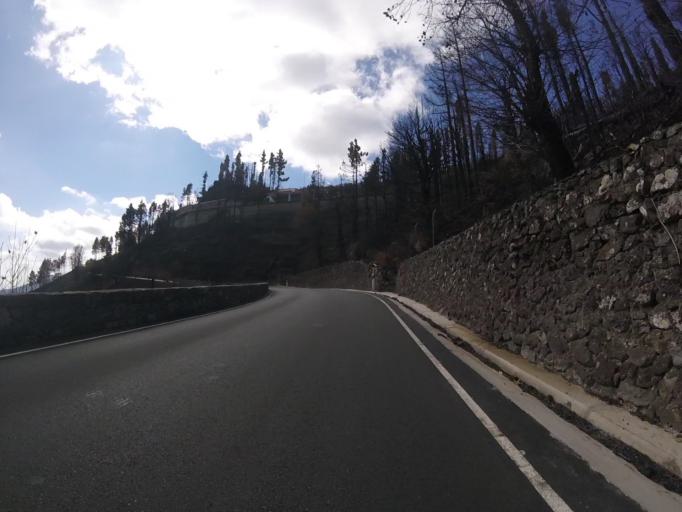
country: ES
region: Canary Islands
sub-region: Provincia de Las Palmas
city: Tejeda
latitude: 28.0038
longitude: -15.5962
